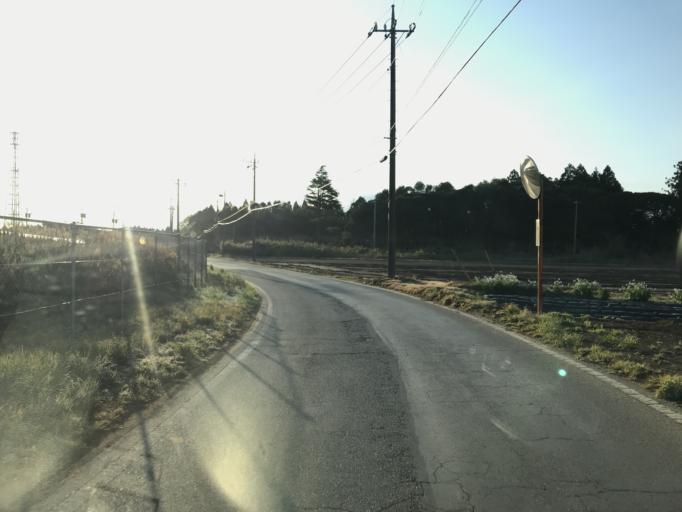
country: JP
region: Chiba
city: Yokaichiba
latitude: 35.7695
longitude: 140.5410
